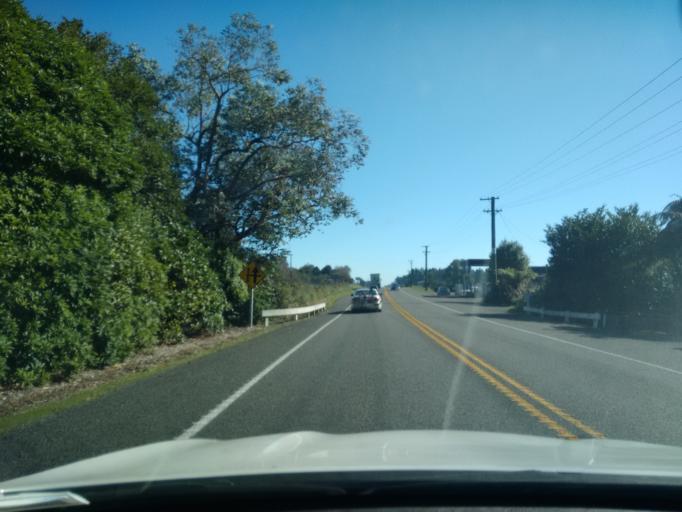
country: NZ
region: Taranaki
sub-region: South Taranaki District
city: Eltham
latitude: -39.2356
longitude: 174.2439
